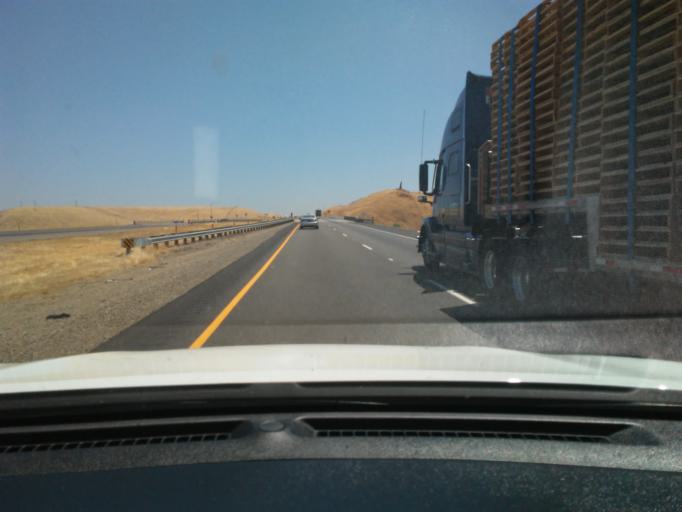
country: US
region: California
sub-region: Stanislaus County
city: Patterson
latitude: 37.3984
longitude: -121.1392
